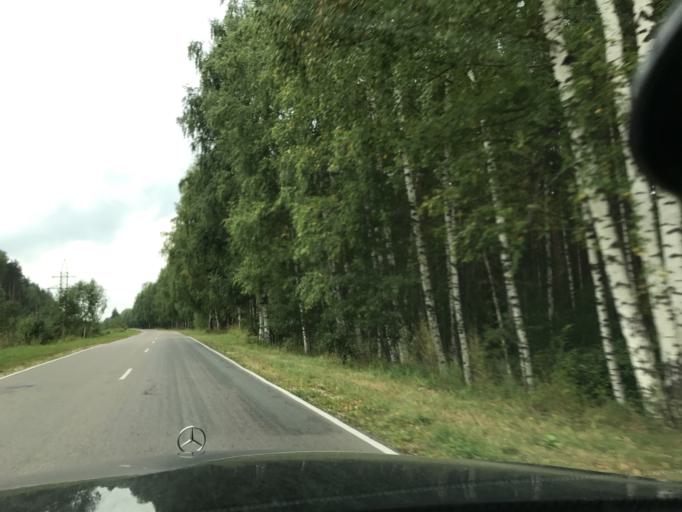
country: RU
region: Nizjnij Novgorod
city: Taremskoye
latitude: 56.0087
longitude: 42.9236
